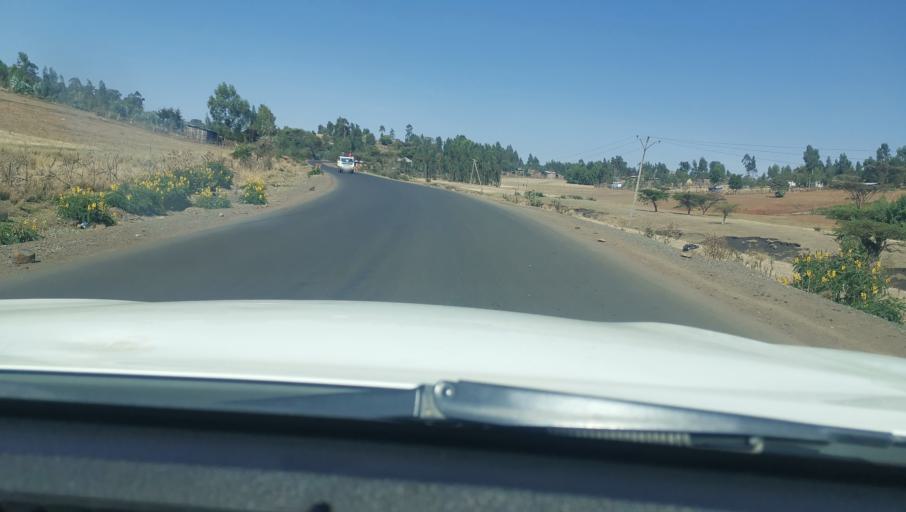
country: ET
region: Oromiya
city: Gedo
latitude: 8.9666
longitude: 37.5273
